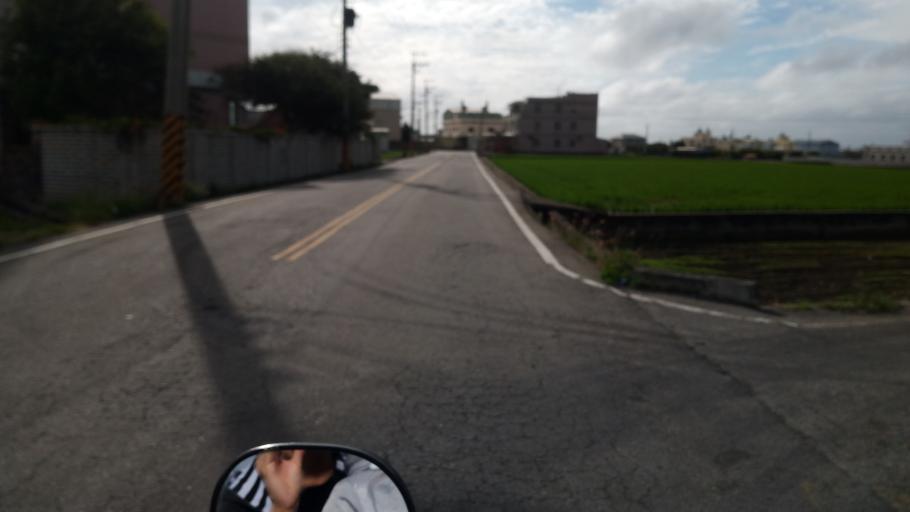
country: TW
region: Taiwan
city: Fengyuan
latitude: 24.4181
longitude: 120.6537
